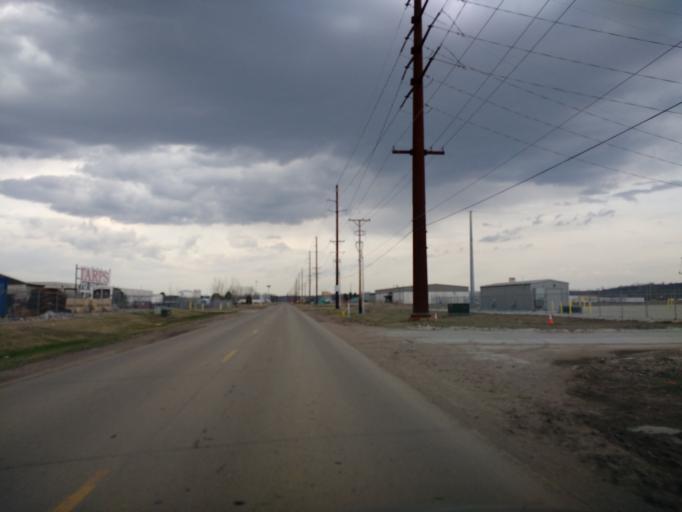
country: US
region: Iowa
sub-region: Woodbury County
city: Sergeant Bluff
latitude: 42.4166
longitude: -96.3699
